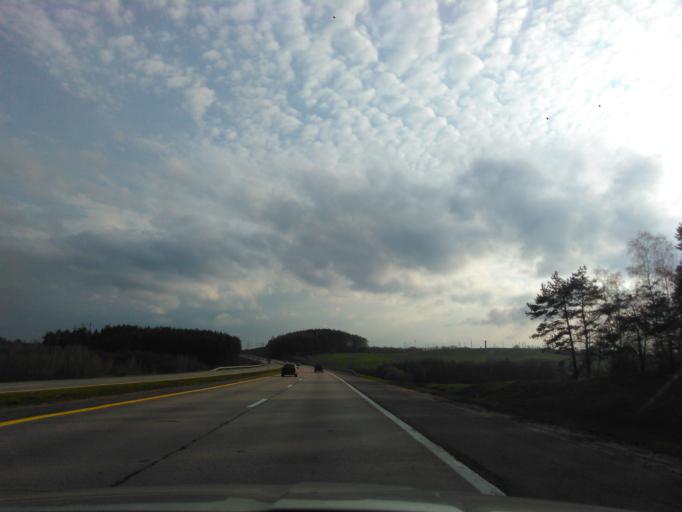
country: BY
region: Minsk
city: Astrashytski Haradok
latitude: 54.0681
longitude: 27.7197
